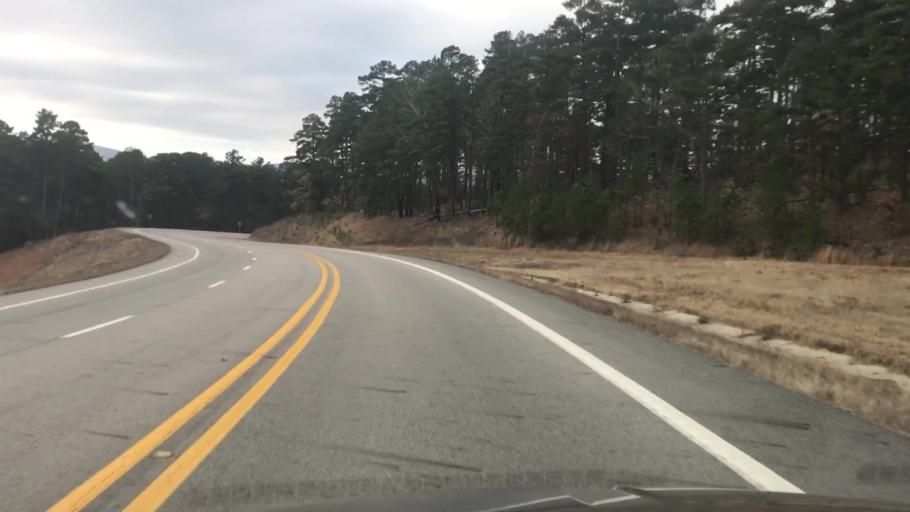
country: US
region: Arkansas
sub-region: Montgomery County
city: Mount Ida
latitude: 34.6828
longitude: -93.7941
